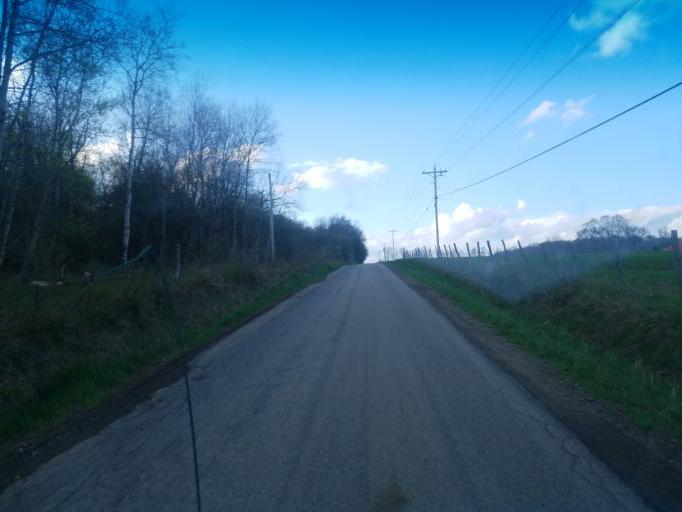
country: US
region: New York
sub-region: Allegany County
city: Andover
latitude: 41.9697
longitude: -77.7592
